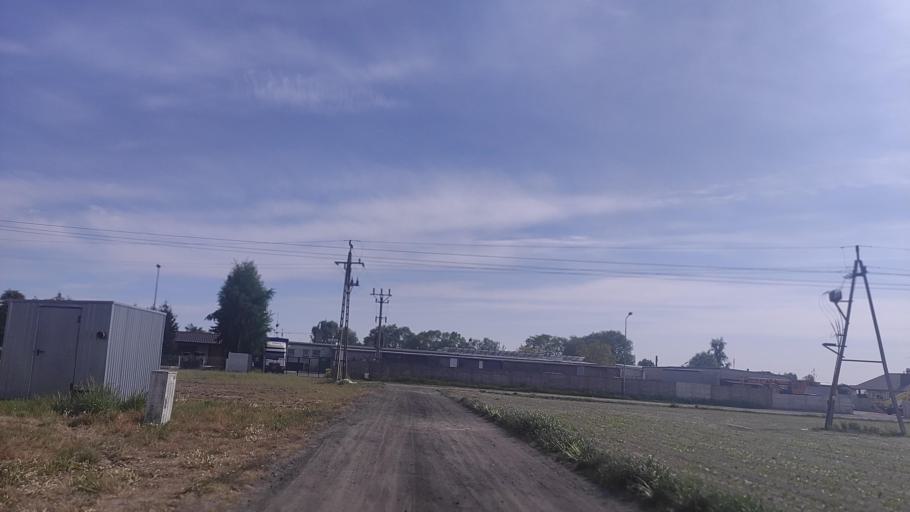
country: PL
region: Greater Poland Voivodeship
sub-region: Powiat poznanski
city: Swarzedz
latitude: 52.4142
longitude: 17.1091
